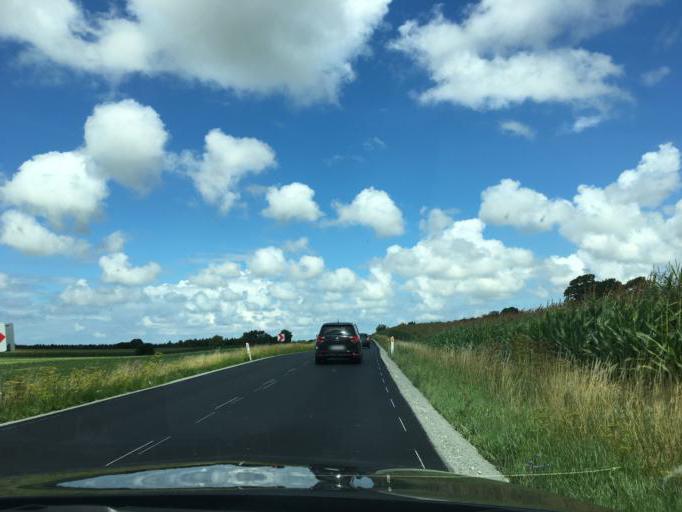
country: DK
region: Capital Region
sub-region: Gribskov Kommune
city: Helsinge
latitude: 56.0378
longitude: 12.2006
